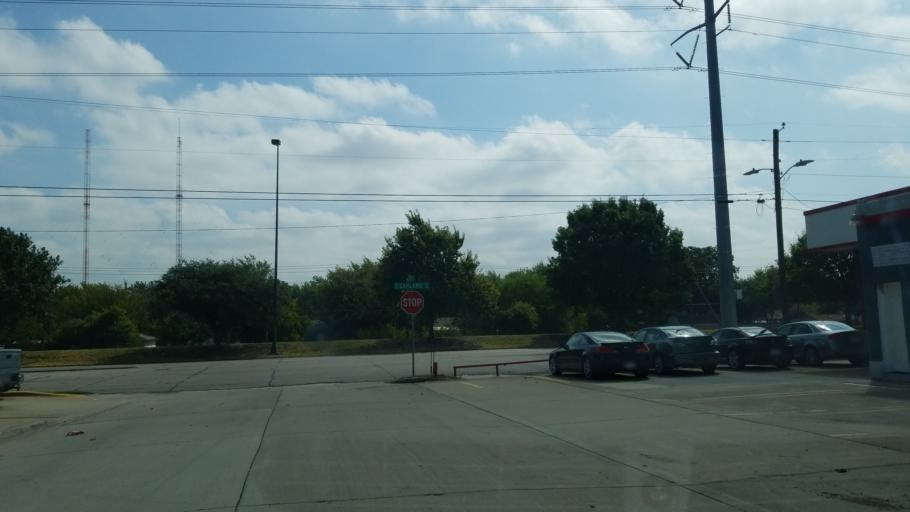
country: US
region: Texas
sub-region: Dallas County
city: Garland
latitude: 32.8923
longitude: -96.6516
